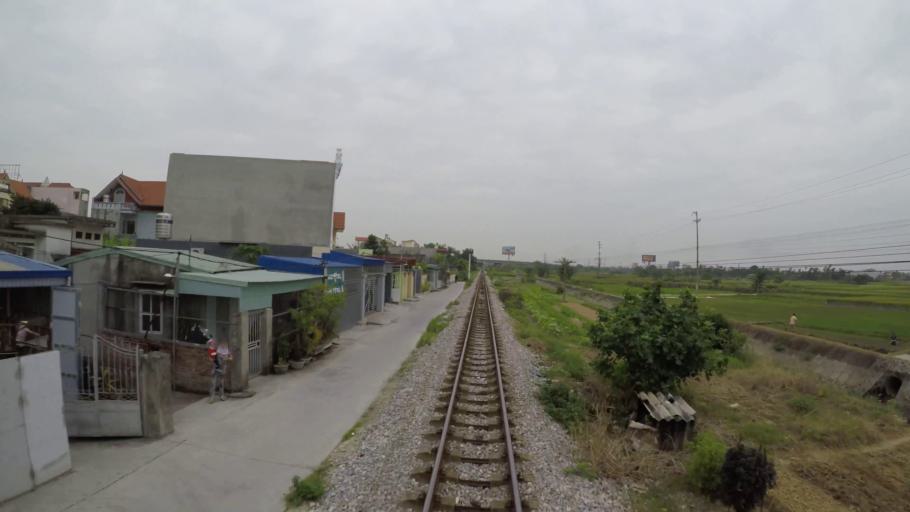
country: VN
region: Hai Phong
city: An Duong
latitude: 20.9131
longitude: 106.5673
